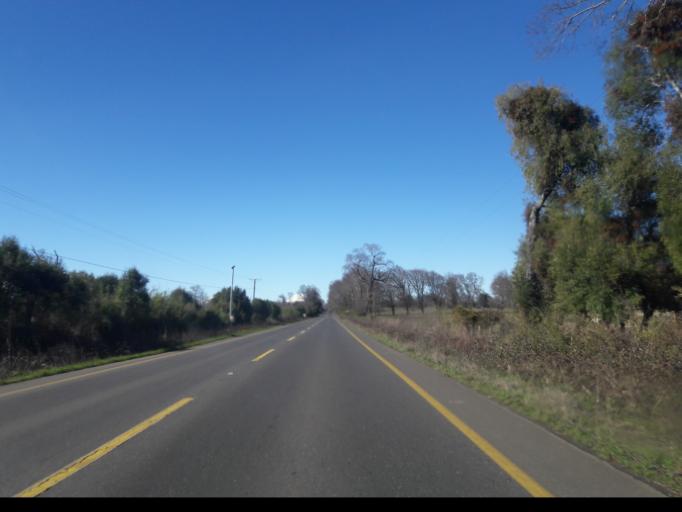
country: CL
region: Araucania
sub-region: Provincia de Malleco
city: Victoria
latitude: -38.2671
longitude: -72.2235
